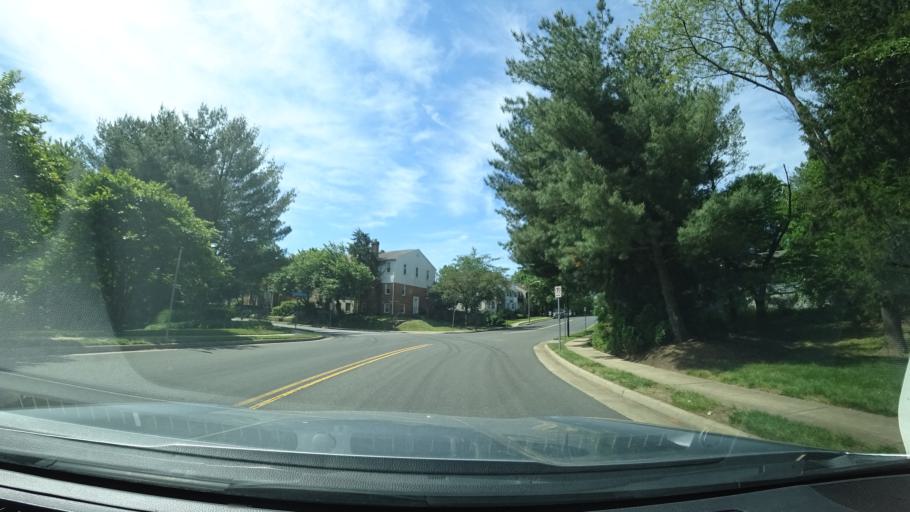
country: US
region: Virginia
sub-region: Fairfax County
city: Herndon
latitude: 38.9770
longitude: -77.3912
